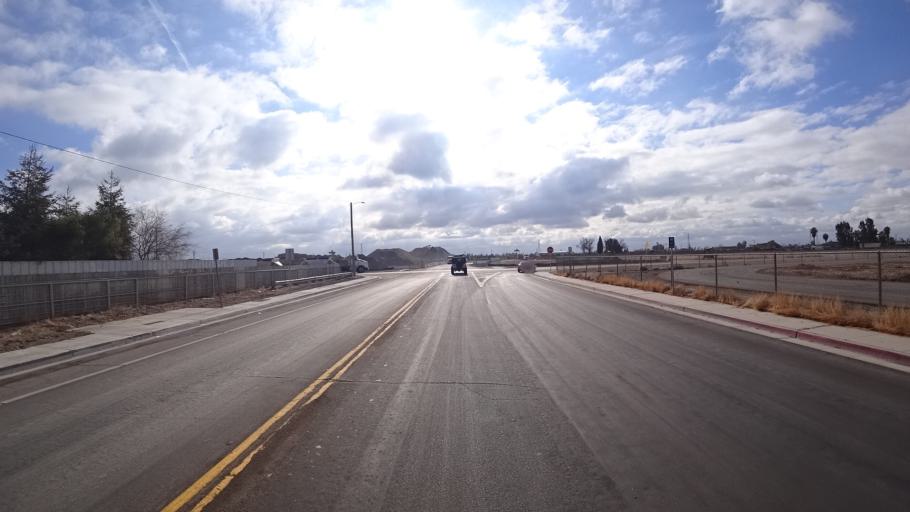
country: US
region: California
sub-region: Kern County
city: Greenfield
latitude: 35.3182
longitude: -118.9938
